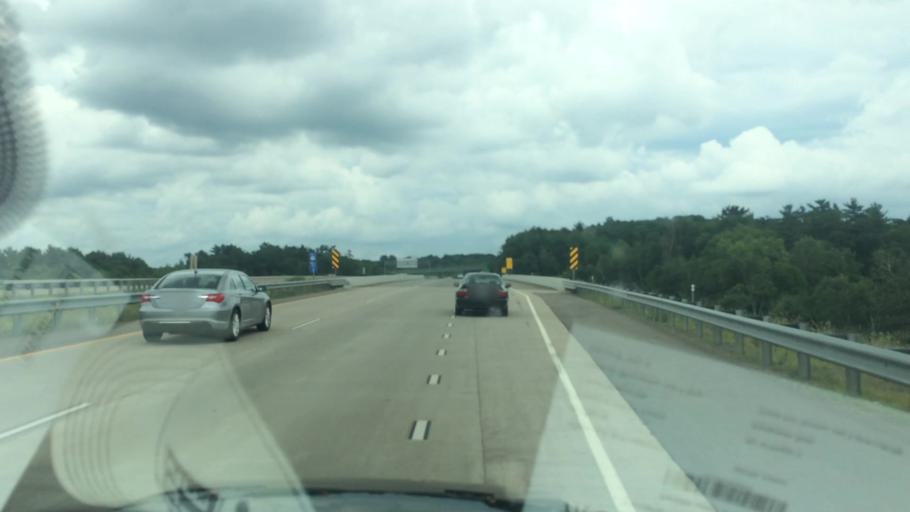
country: US
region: Wisconsin
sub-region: Marathon County
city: Rothschild
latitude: 44.8965
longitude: -89.6169
